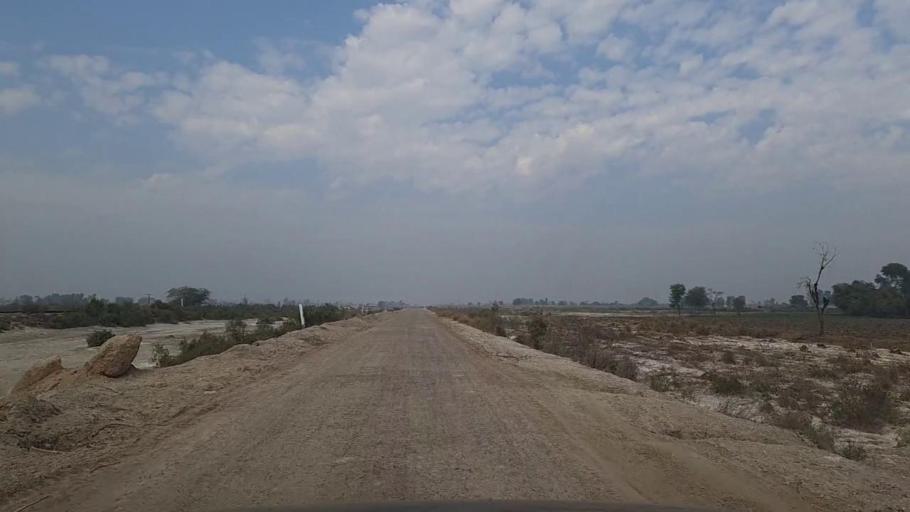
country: PK
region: Sindh
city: Daur
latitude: 26.3661
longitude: 68.3608
